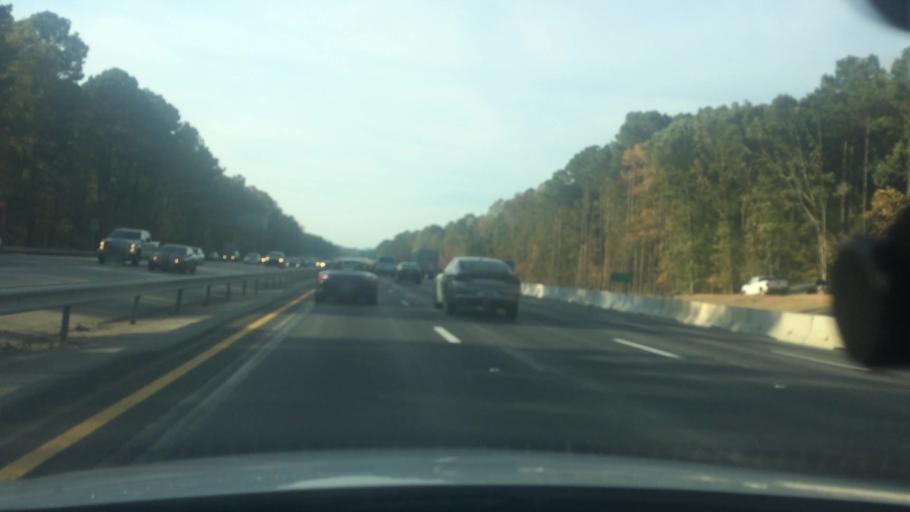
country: US
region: North Carolina
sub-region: Wake County
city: Morrisville
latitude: 35.8560
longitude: -78.8068
